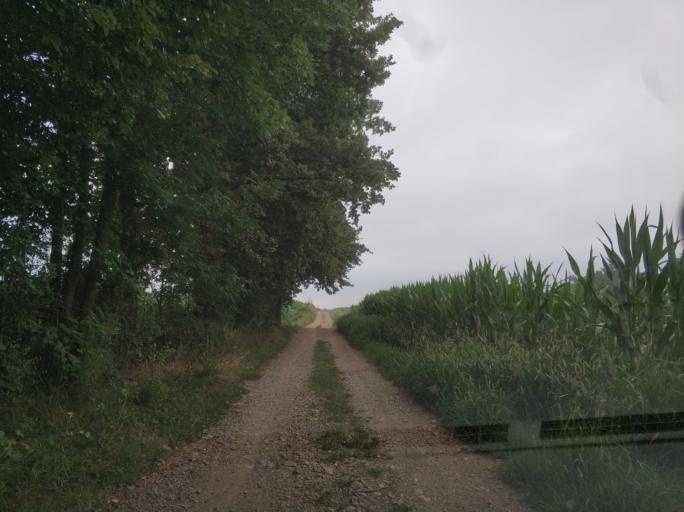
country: IT
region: Piedmont
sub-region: Provincia di Torino
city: San Francesco al Campo
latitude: 45.2272
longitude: 7.6853
